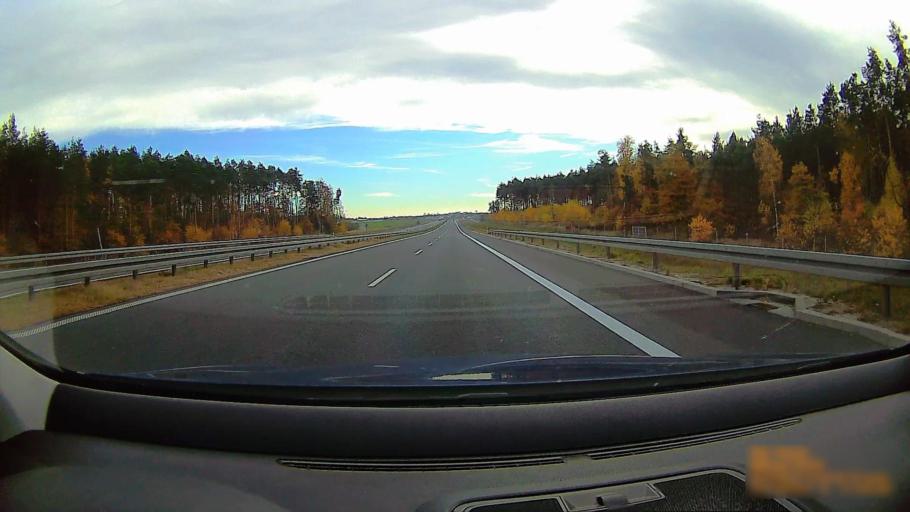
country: PL
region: Greater Poland Voivodeship
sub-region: Powiat ostrowski
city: Ostrow Wielkopolski
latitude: 51.6525
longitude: 17.8684
